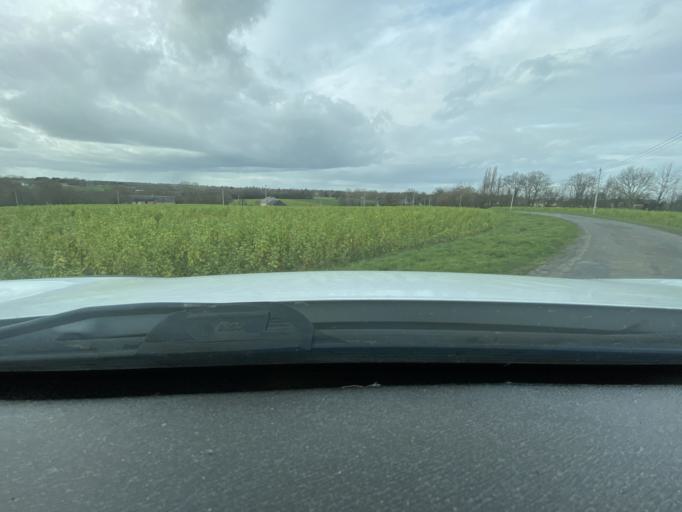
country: FR
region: Brittany
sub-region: Departement d'Ille-et-Vilaine
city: Melesse
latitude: 48.2210
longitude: -1.7080
